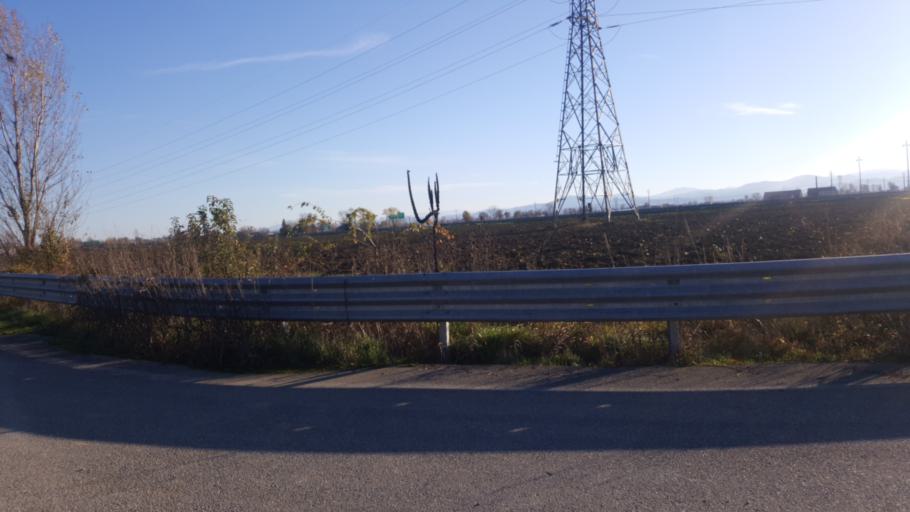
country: IT
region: Emilia-Romagna
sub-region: Provincia di Piacenza
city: Roveleto
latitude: 44.9706
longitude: 9.8922
